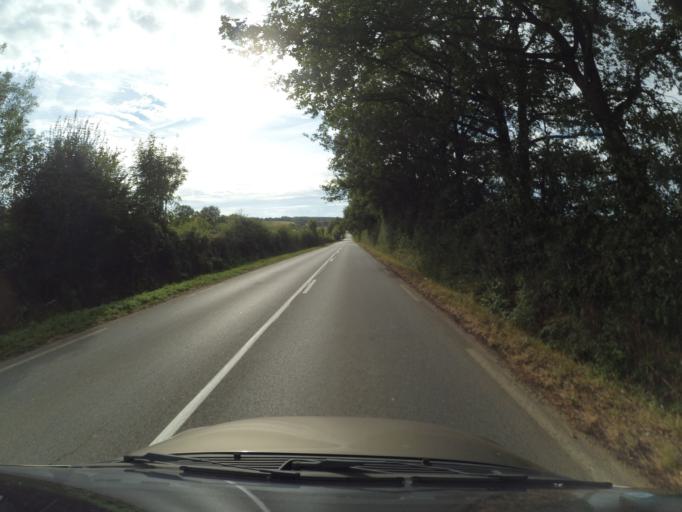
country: FR
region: Poitou-Charentes
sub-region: Departement des Deux-Sevres
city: Saint-Amand-sur-Sevre
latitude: 46.9270
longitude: -0.7681
